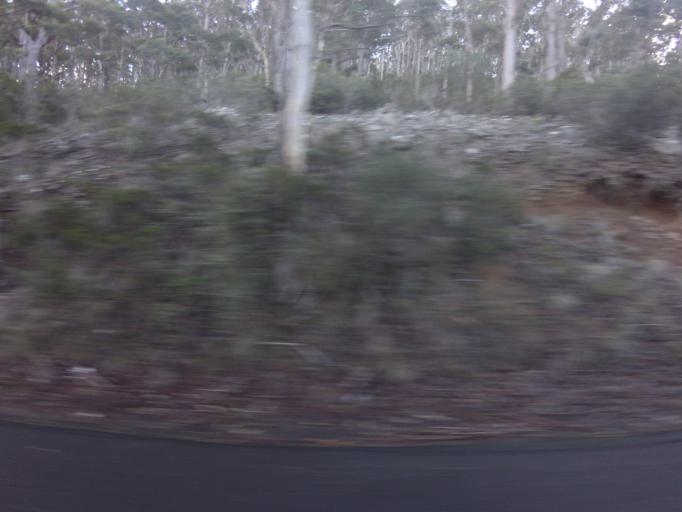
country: AU
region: Tasmania
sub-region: Glenorchy
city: Berriedale
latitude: -42.8204
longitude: 147.1875
